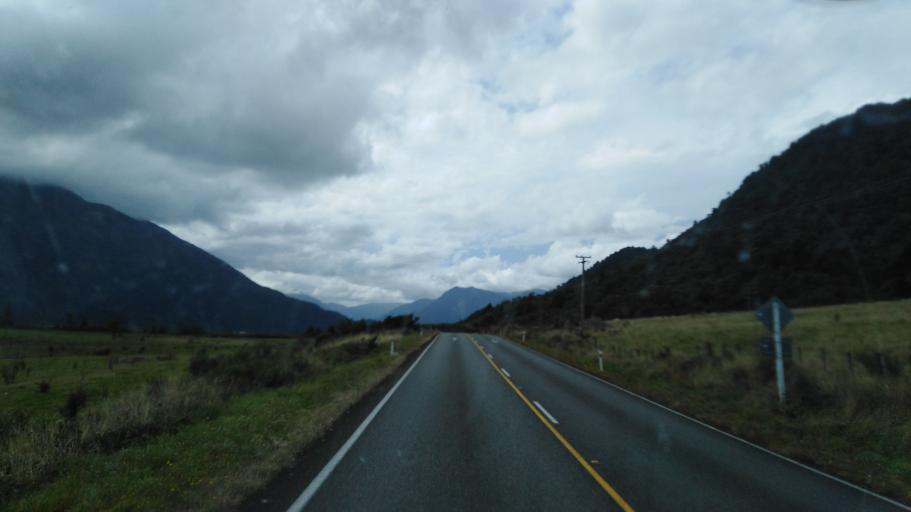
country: NZ
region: West Coast
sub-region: Grey District
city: Greymouth
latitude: -42.7297
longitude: 171.2688
